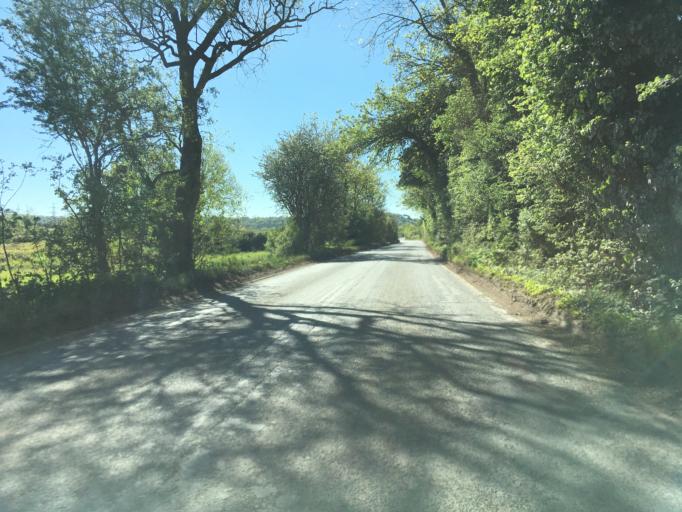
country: GB
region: England
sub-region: South Gloucestershire
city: Severn Beach
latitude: 51.5287
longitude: -2.6621
